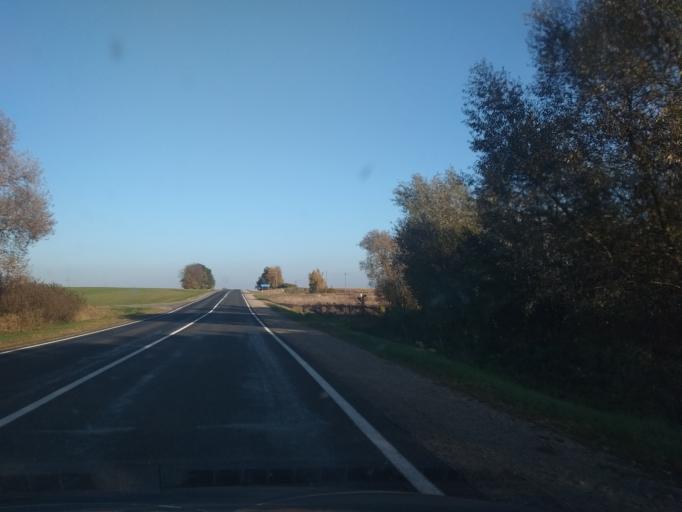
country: BY
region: Grodnenskaya
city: Svislach
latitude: 53.1338
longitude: 24.2265
